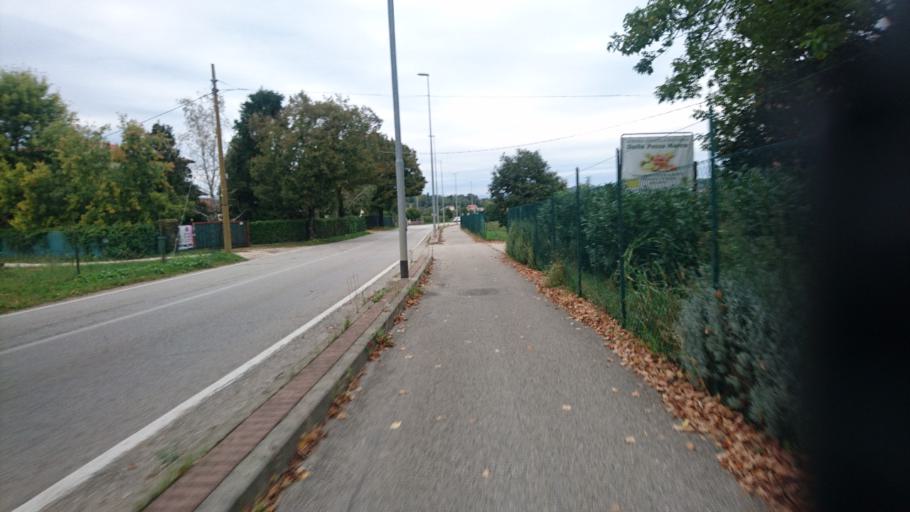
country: IT
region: Veneto
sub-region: Provincia di Vicenza
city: Tavernelle
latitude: 45.5139
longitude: 11.4291
